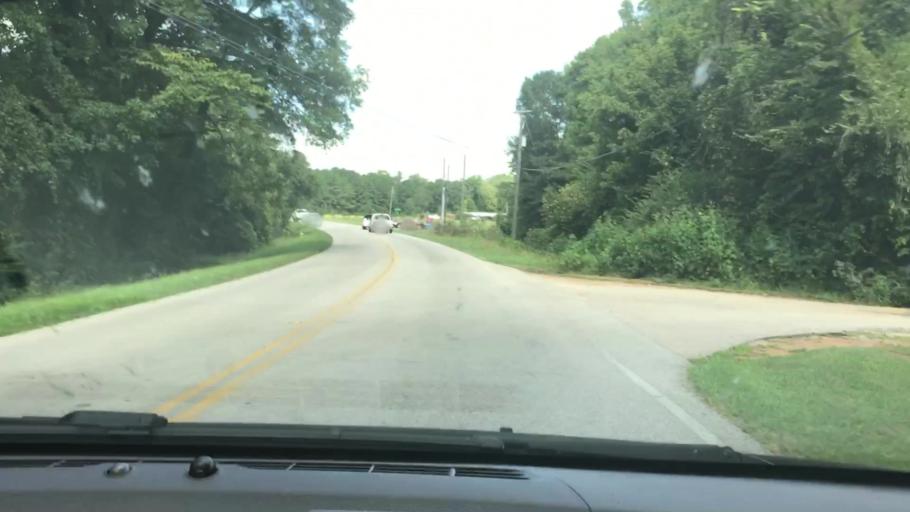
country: US
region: Georgia
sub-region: Troup County
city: La Grange
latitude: 33.0167
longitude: -85.0676
